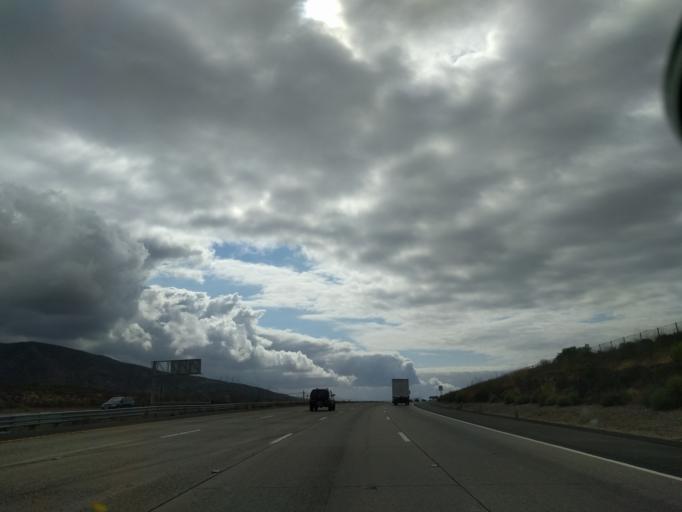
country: US
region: California
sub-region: Orange County
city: San Clemente
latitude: 33.3781
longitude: -117.5652
